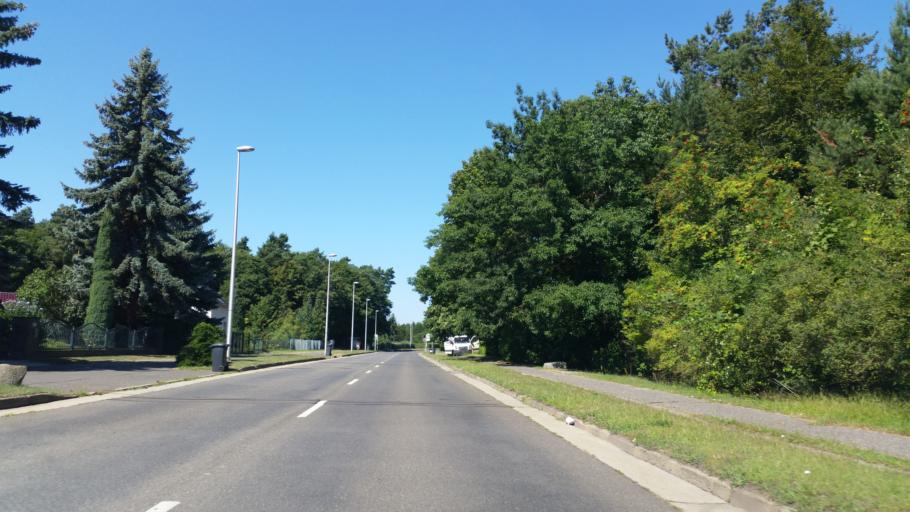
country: DE
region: Brandenburg
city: Cottbus
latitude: 51.7295
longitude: 14.3152
